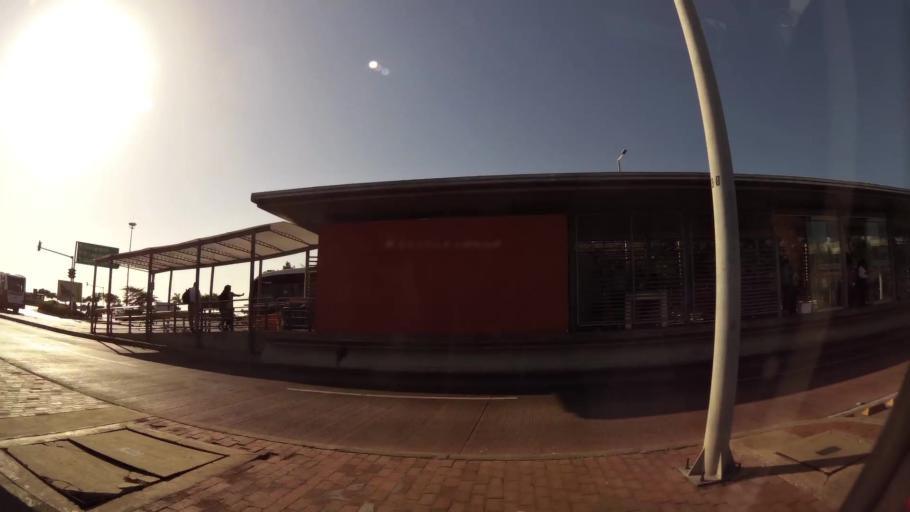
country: CO
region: Bolivar
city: Cartagena
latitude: 10.4197
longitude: -75.5516
